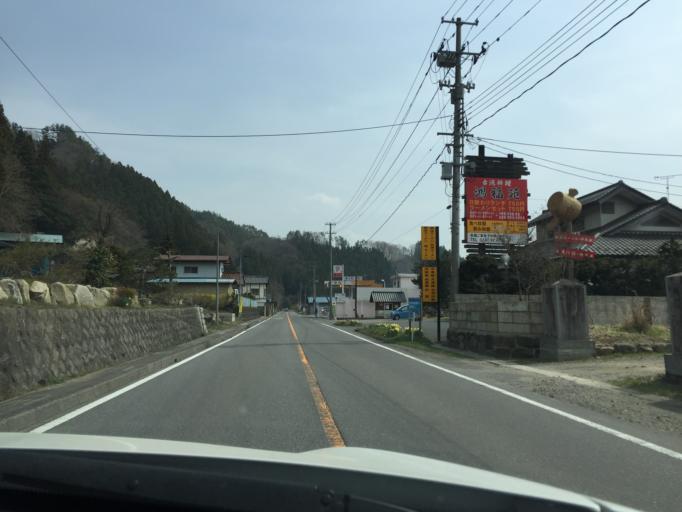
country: JP
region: Fukushima
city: Ishikawa
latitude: 37.0820
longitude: 140.5719
